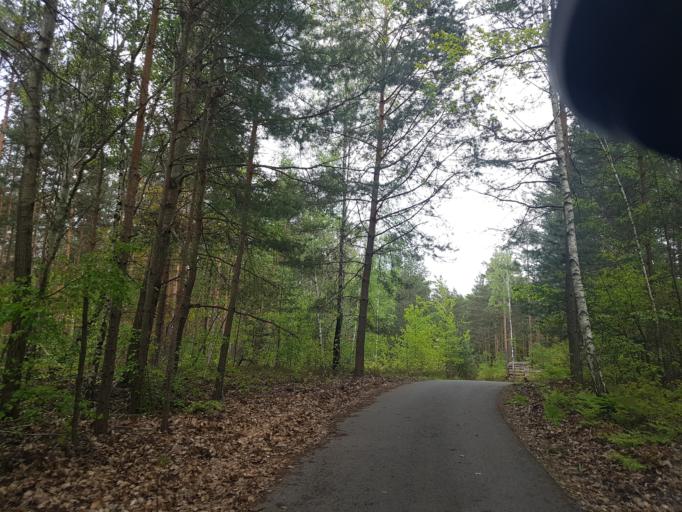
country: DE
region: Saxony
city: Gross Duben
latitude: 51.6084
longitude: 14.5793
